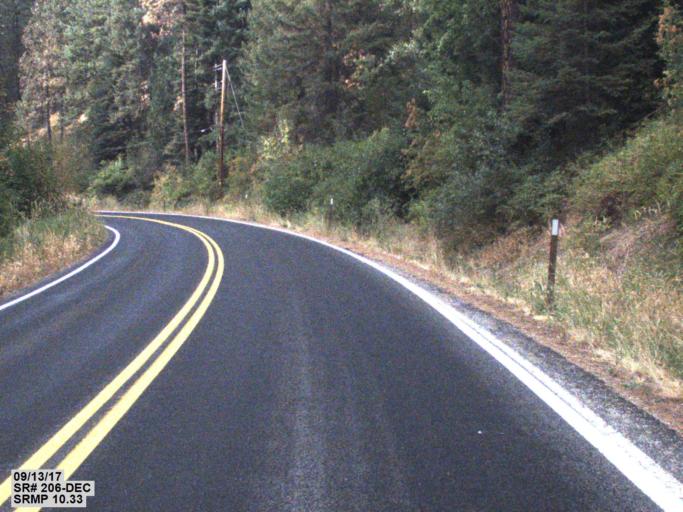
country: US
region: Washington
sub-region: Spokane County
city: Trentwood
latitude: 47.8369
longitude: -117.1838
